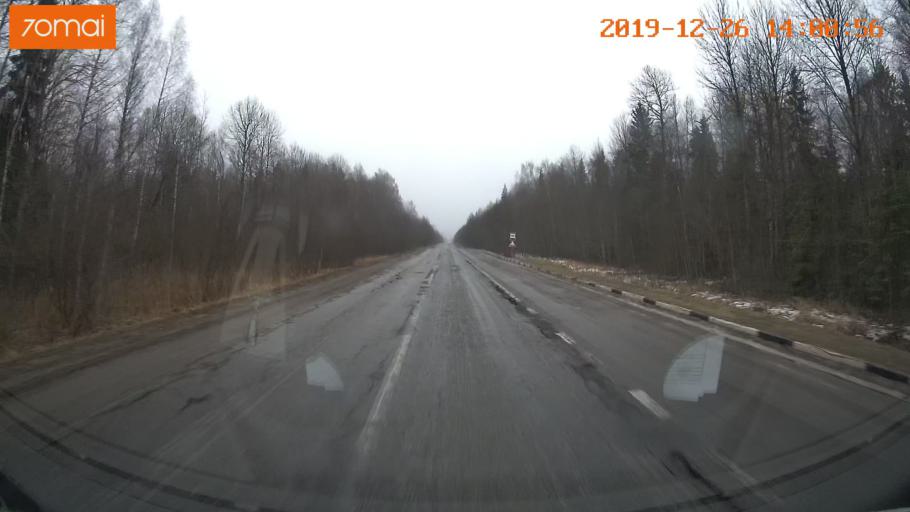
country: RU
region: Jaroslavl
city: Poshekhon'ye
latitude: 58.5544
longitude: 38.7534
